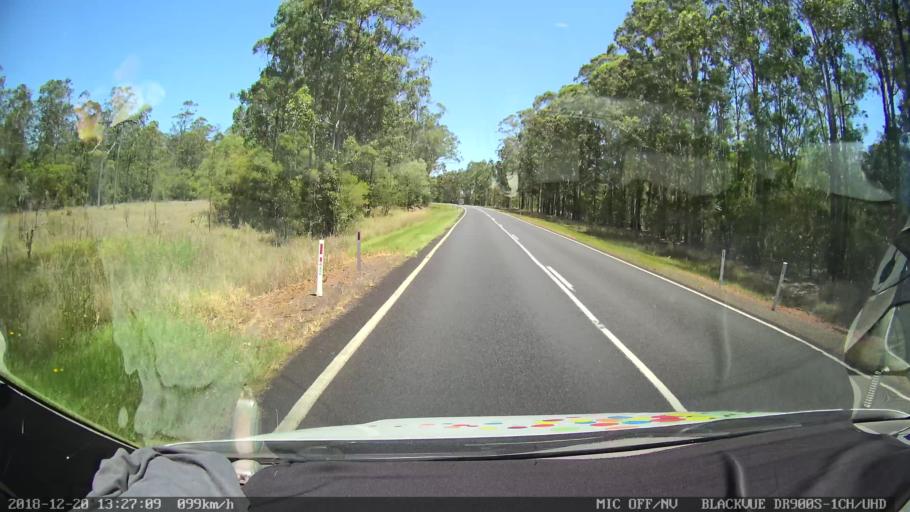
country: AU
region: New South Wales
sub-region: Richmond Valley
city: Casino
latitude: -29.1559
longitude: 152.9926
